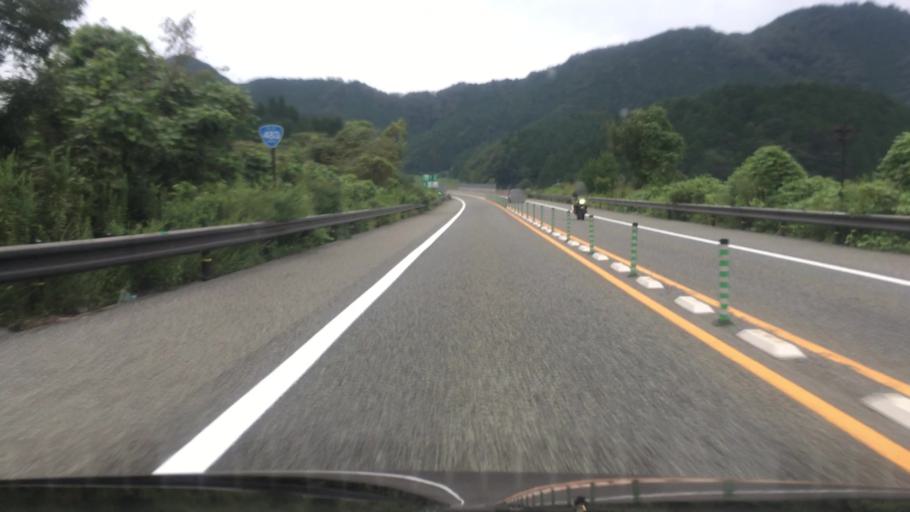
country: JP
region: Kyoto
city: Fukuchiyama
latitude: 35.3077
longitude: 134.8775
